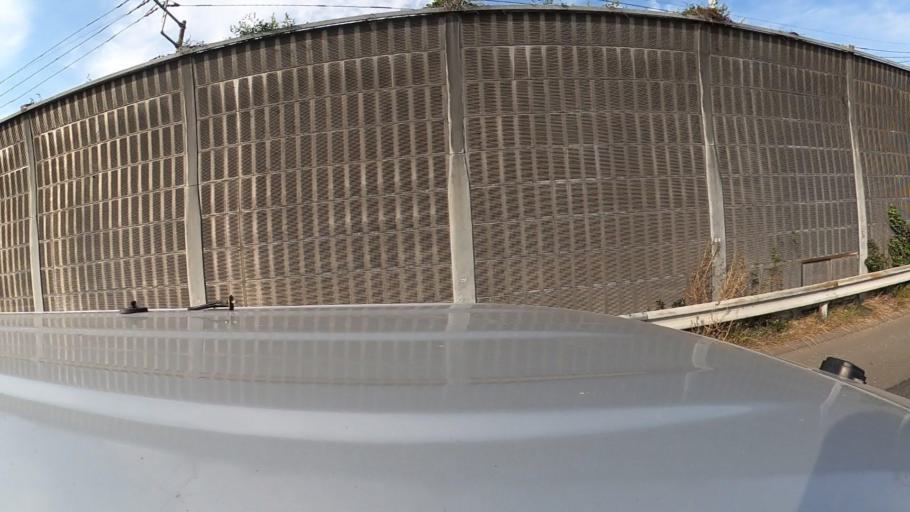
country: JP
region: Saitama
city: Kawagoe
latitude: 35.8856
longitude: 139.4688
